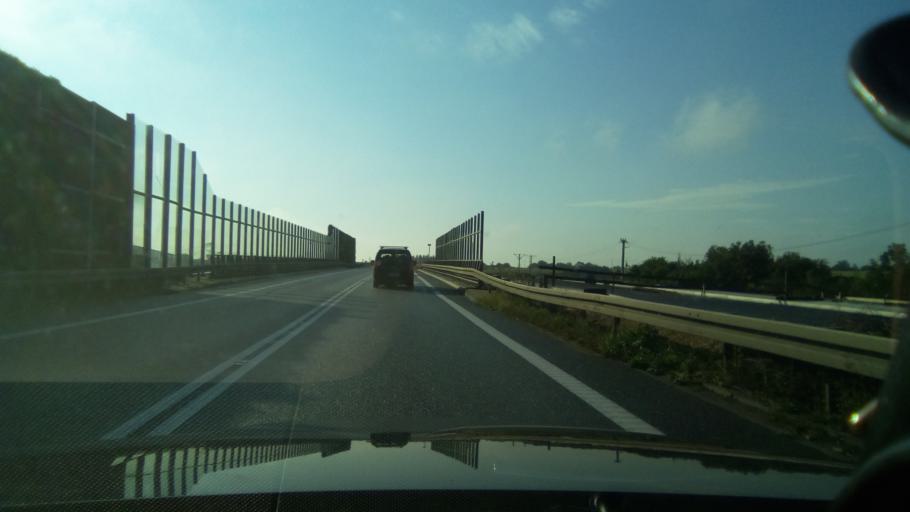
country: PL
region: Silesian Voivodeship
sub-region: Powiat bedzinski
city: Mierzecice
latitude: 50.4473
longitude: 19.1372
